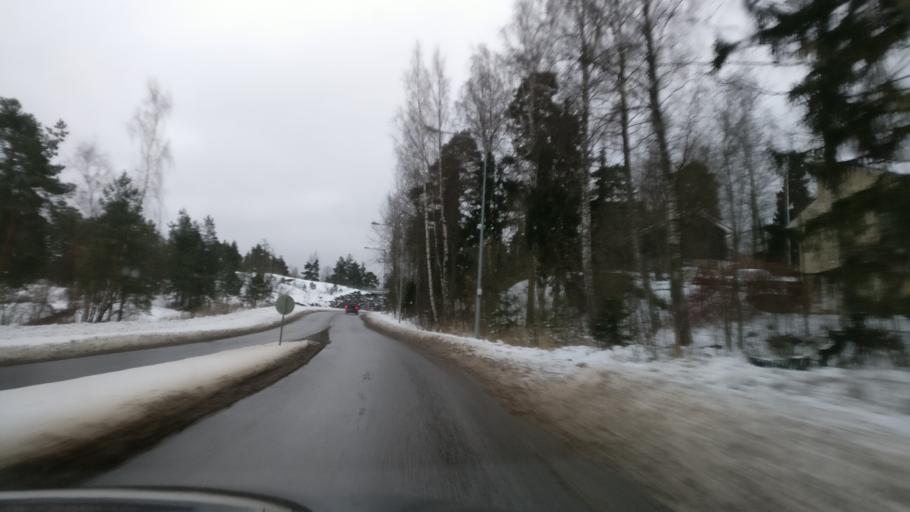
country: FI
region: Uusimaa
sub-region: Helsinki
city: Helsinki
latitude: 60.1747
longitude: 25.0494
